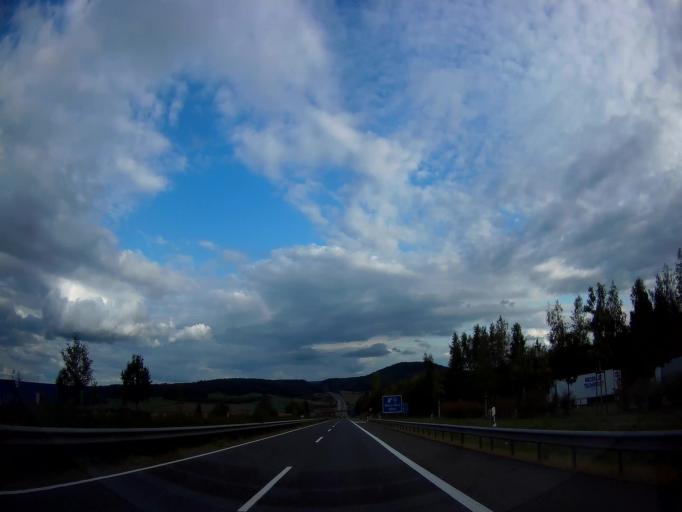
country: DE
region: Rheinland-Pfalz
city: Bergweiler
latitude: 49.9689
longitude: 6.8359
